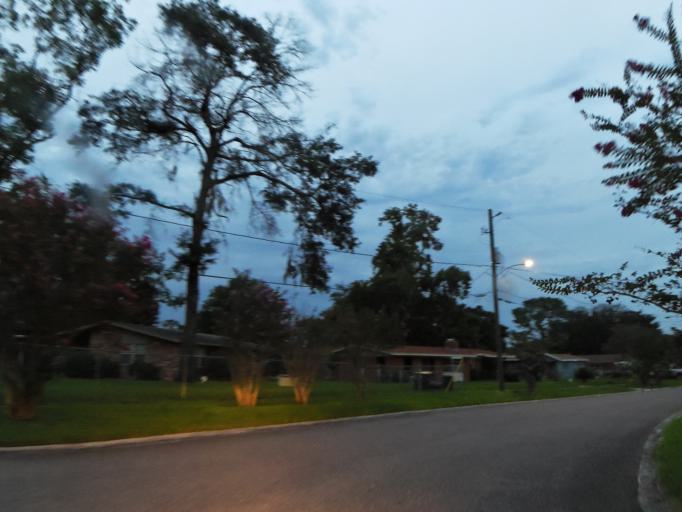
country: US
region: Florida
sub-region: Duval County
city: Jacksonville
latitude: 30.3076
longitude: -81.7748
